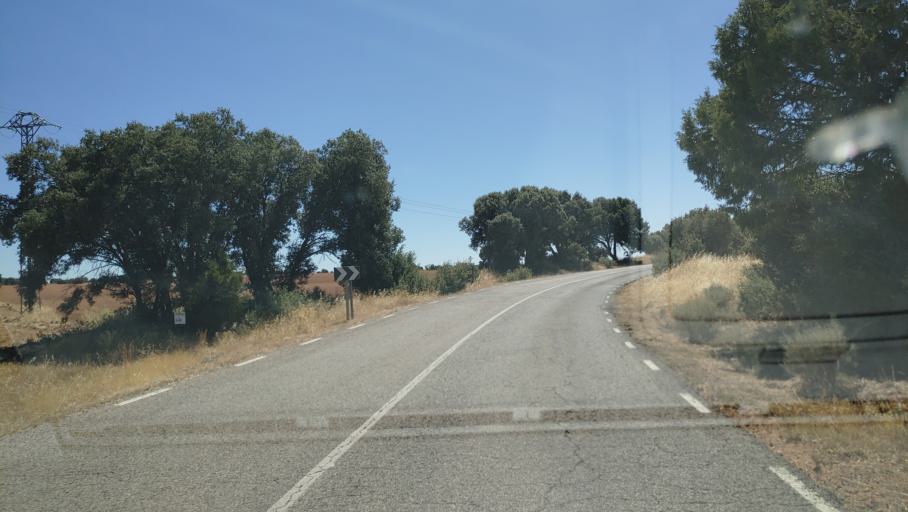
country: ES
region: Castille-La Mancha
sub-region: Provincia de Albacete
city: Ossa de Montiel
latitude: 38.9229
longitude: -2.7547
